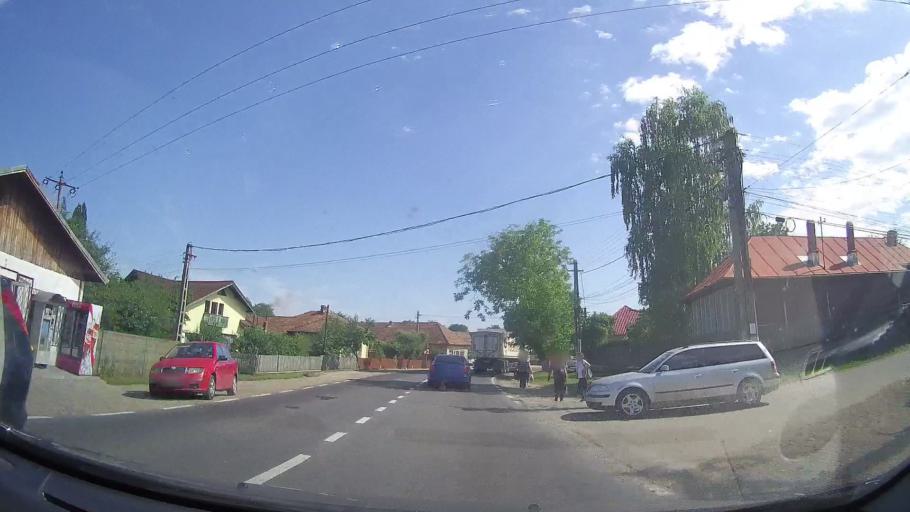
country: RO
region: Prahova
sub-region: Comuna Izvoarele
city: Homoraciu
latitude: 45.2678
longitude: 26.0150
